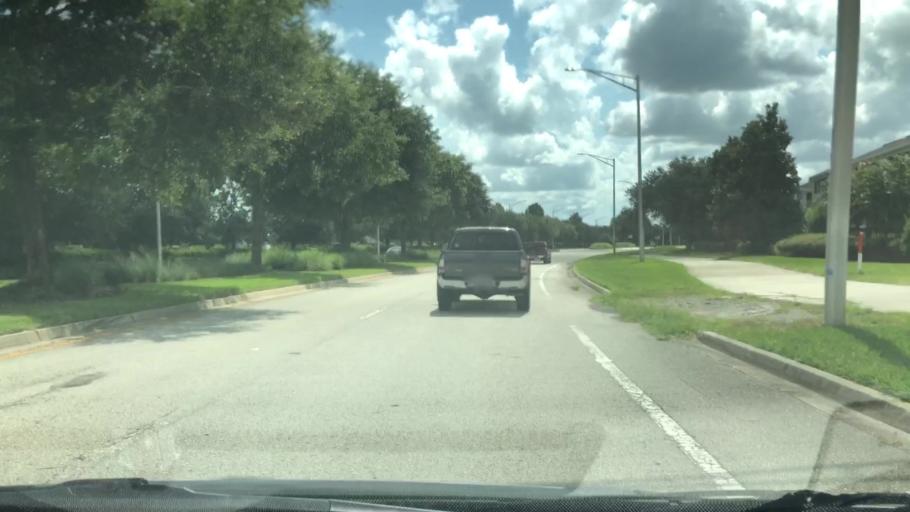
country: US
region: Florida
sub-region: Saint Johns County
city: Fruit Cove
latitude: 30.1289
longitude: -81.5389
